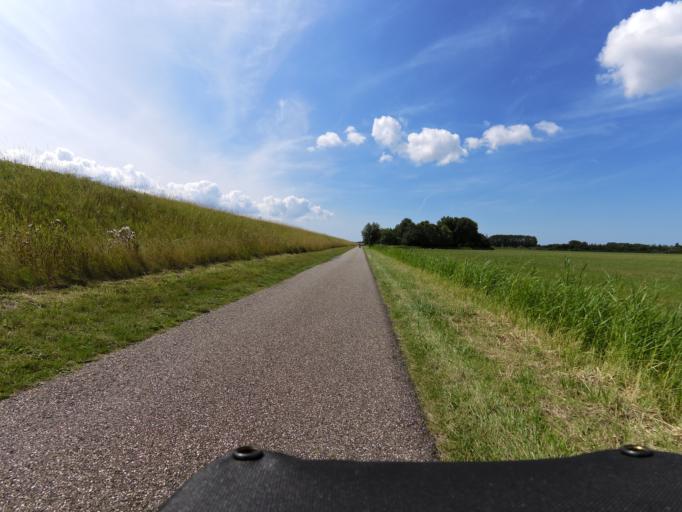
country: NL
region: South Holland
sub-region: Gemeente Goeree-Overflakkee
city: Ouddorp
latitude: 51.7980
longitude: 3.9226
